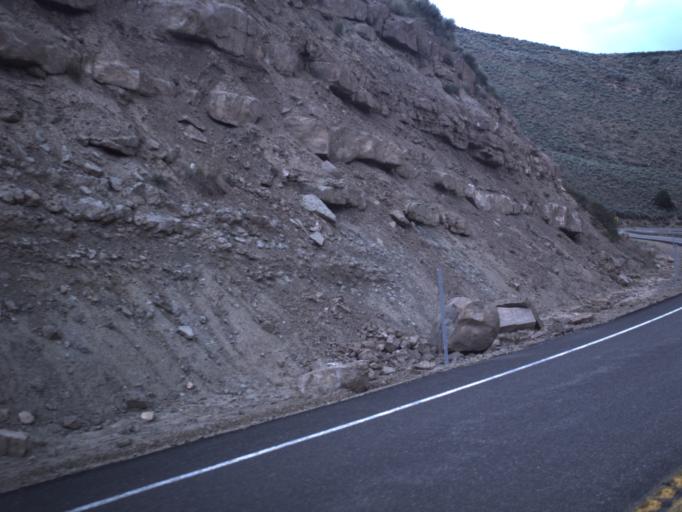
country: US
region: Utah
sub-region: Carbon County
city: Helper
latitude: 39.7869
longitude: -110.7912
